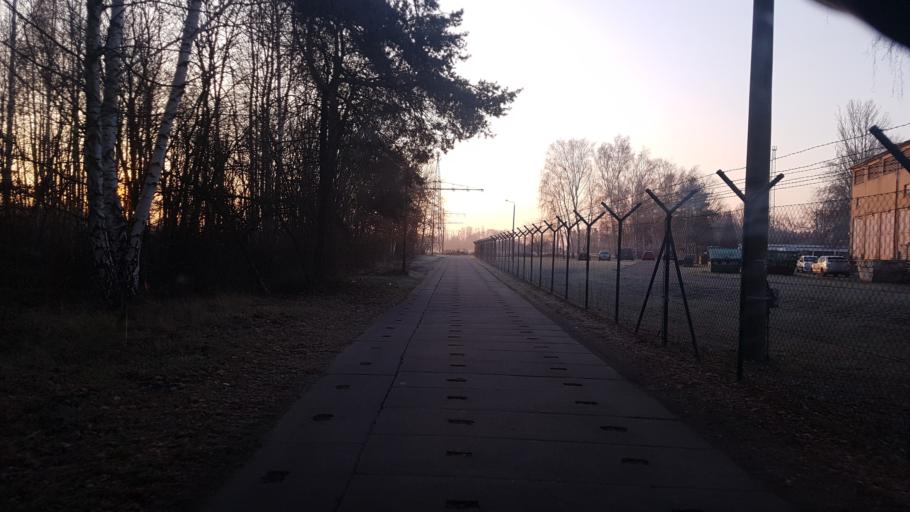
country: DE
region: Brandenburg
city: Lauchhammer
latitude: 51.4814
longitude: 13.7215
